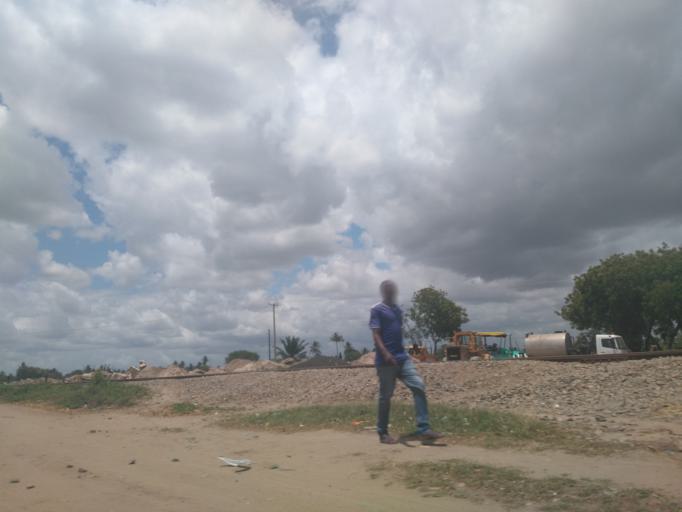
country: TZ
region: Dar es Salaam
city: Dar es Salaam
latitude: -6.8536
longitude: 39.2427
